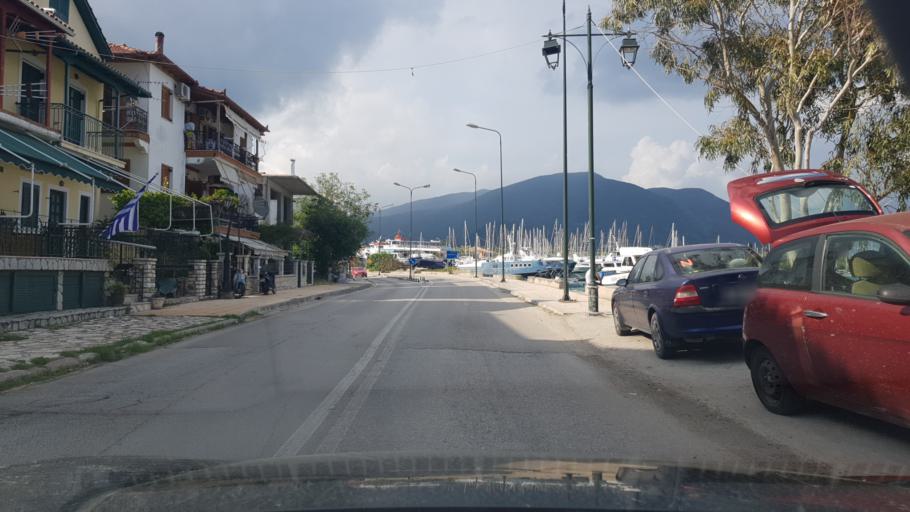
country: GR
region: Ionian Islands
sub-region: Lefkada
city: Nidri
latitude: 38.6888
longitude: 20.6988
